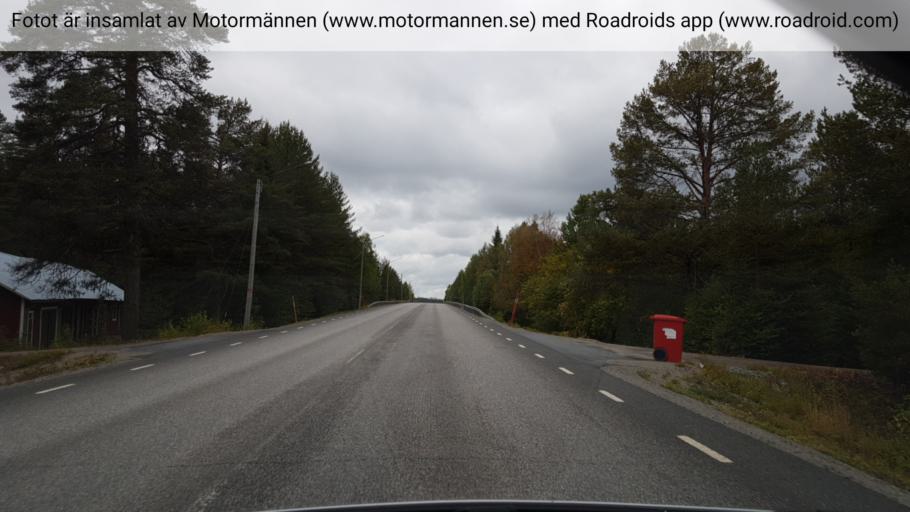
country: SE
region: Vaesterbotten
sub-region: Skelleftea Kommun
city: Langsele
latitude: 64.9322
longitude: 19.9805
